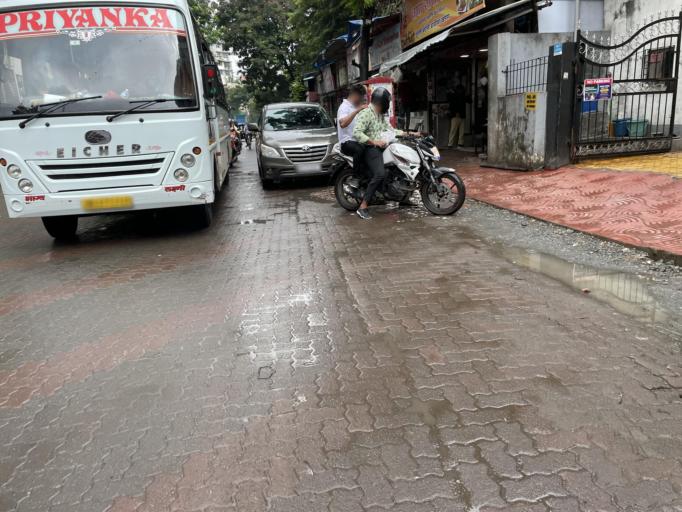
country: IN
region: Maharashtra
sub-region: Mumbai Suburban
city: Borivli
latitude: 19.2547
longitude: 72.8611
